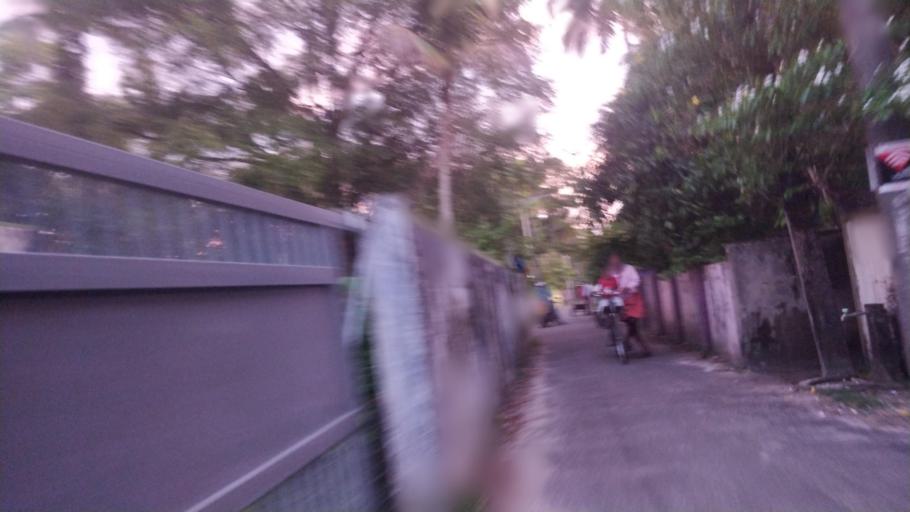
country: IN
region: Kerala
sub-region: Alappuzha
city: Shertallai
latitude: 9.6732
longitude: 76.3390
